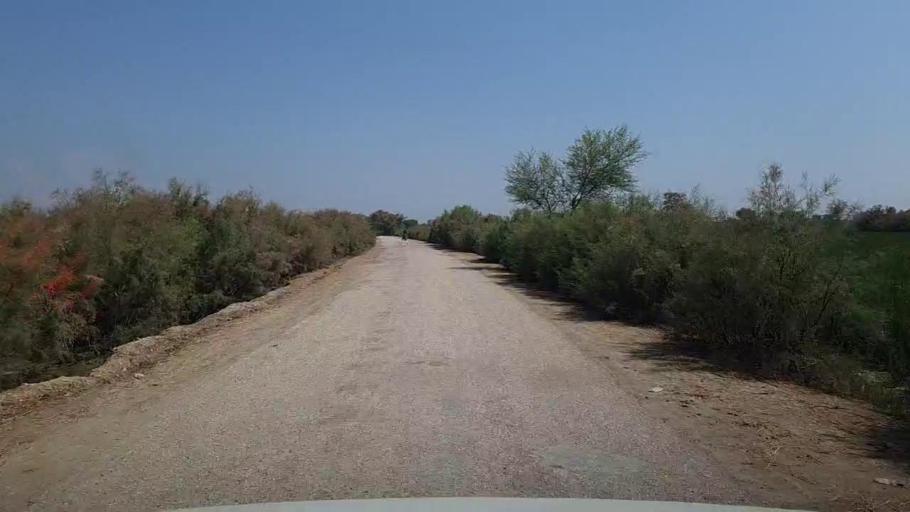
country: PK
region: Sindh
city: Kandhkot
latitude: 28.2786
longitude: 69.3552
